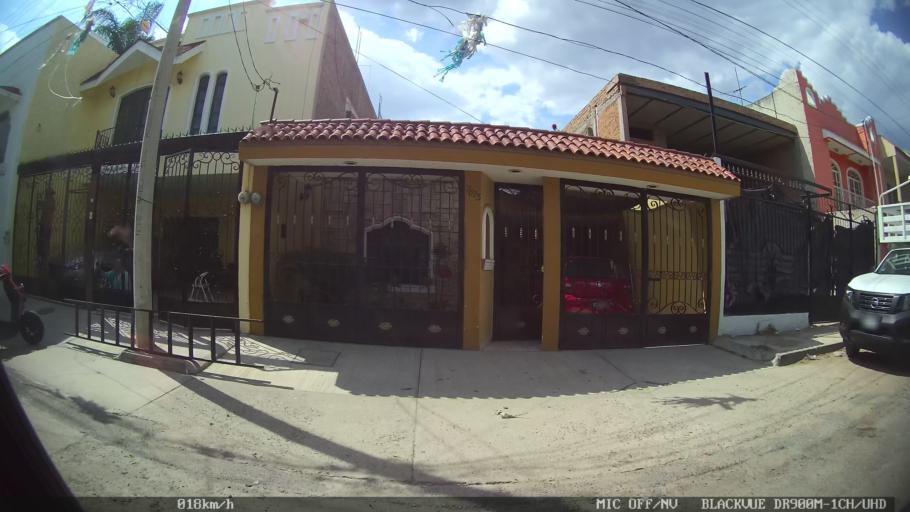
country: MX
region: Jalisco
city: Tlaquepaque
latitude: 20.6270
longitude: -103.2670
